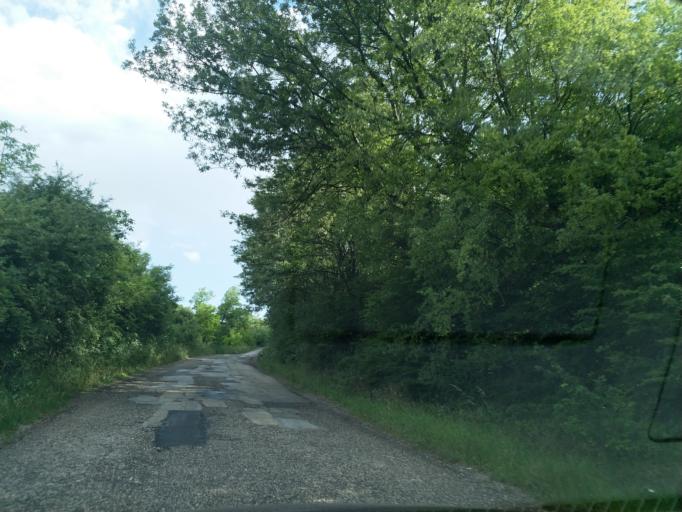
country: RS
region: Central Serbia
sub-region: Borski Okrug
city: Bor
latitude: 43.9947
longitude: 21.9783
